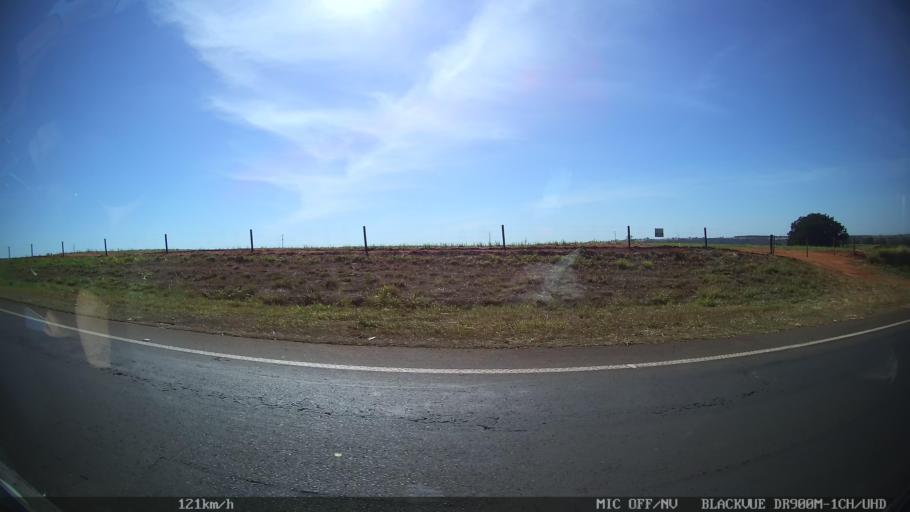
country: BR
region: Sao Paulo
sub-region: Olimpia
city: Olimpia
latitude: -20.6238
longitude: -48.7777
